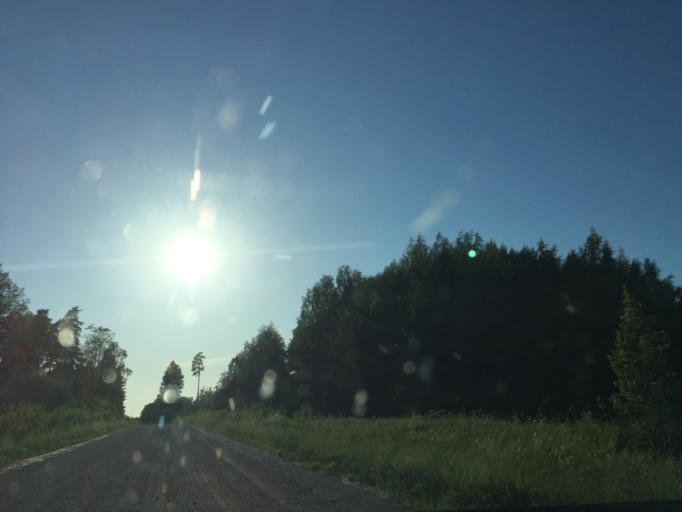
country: LV
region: Talsu Rajons
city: Sabile
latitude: 56.8632
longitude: 22.6606
